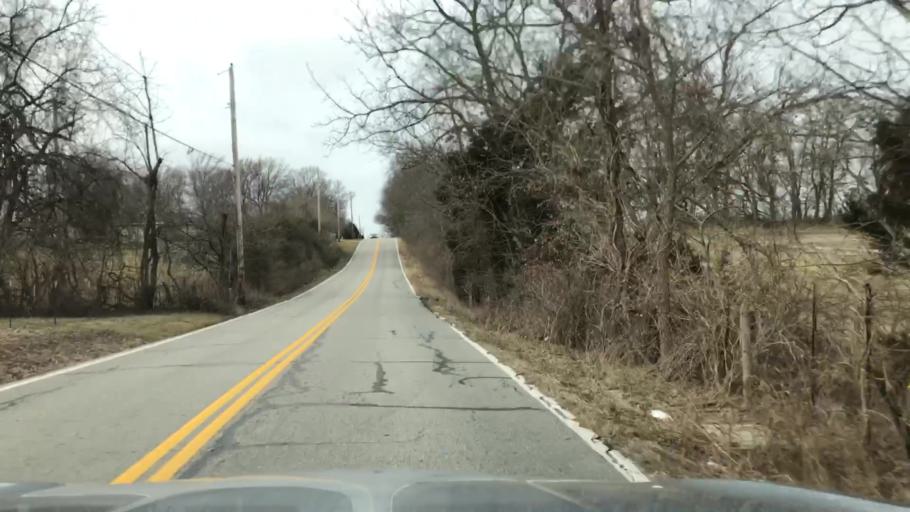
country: US
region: Missouri
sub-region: Jackson County
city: Lees Summit
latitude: 38.8899
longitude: -94.4091
